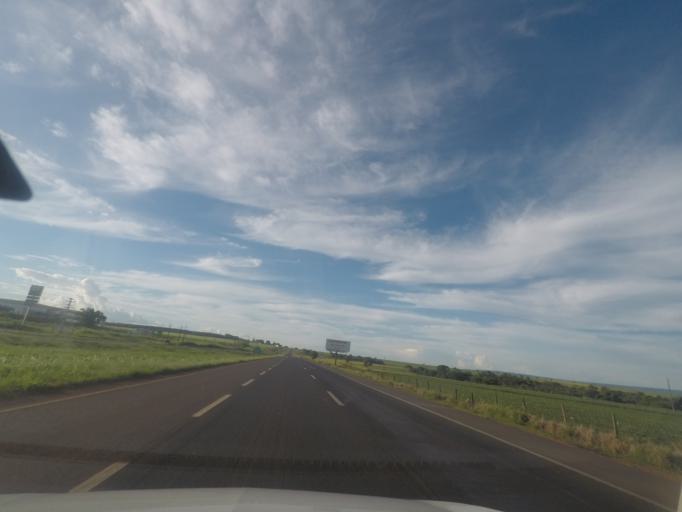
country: BR
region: Goias
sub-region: Itumbiara
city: Itumbiara
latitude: -18.3235
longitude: -49.2278
